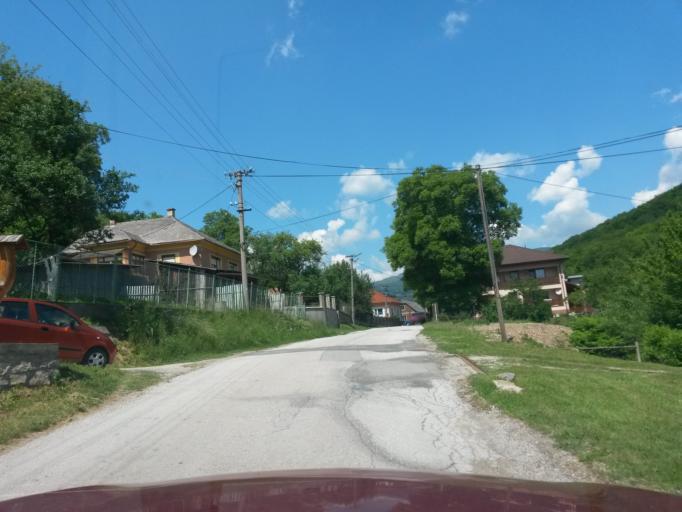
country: SK
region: Kosicky
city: Roznava
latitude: 48.6857
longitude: 20.5422
